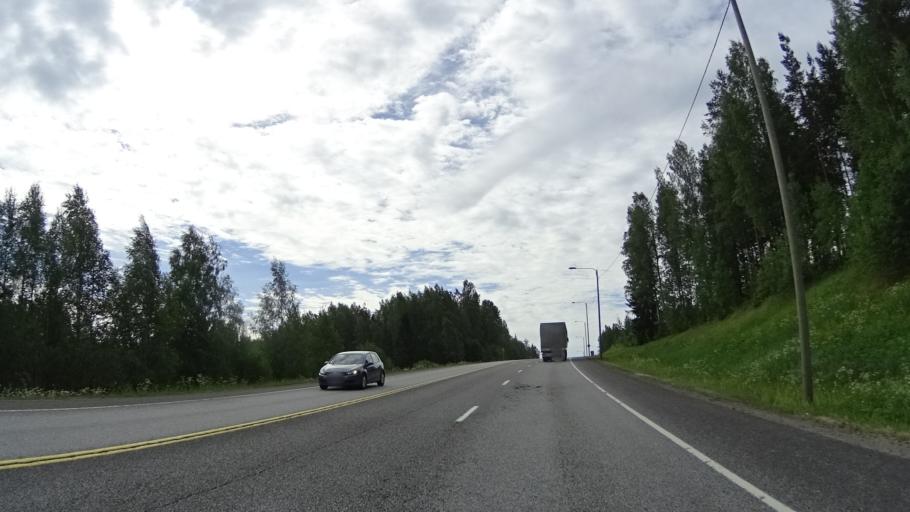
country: FI
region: Uusimaa
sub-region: Helsinki
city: Karkkila
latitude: 60.5112
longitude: 24.2604
